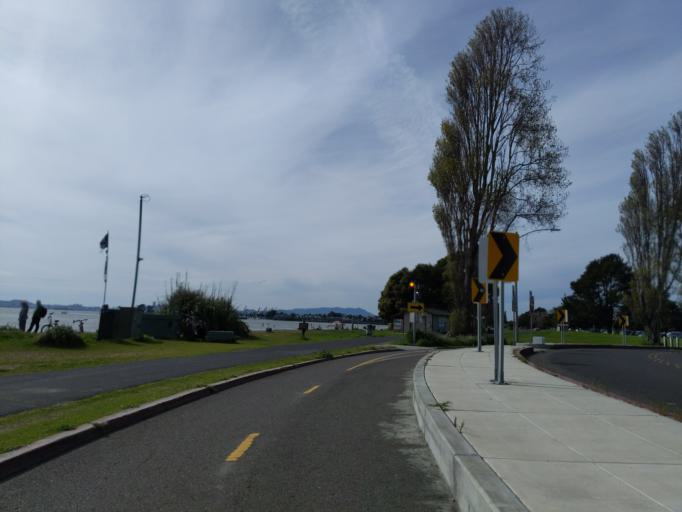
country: US
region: California
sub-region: Alameda County
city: Alameda
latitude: 37.7622
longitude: -122.2713
